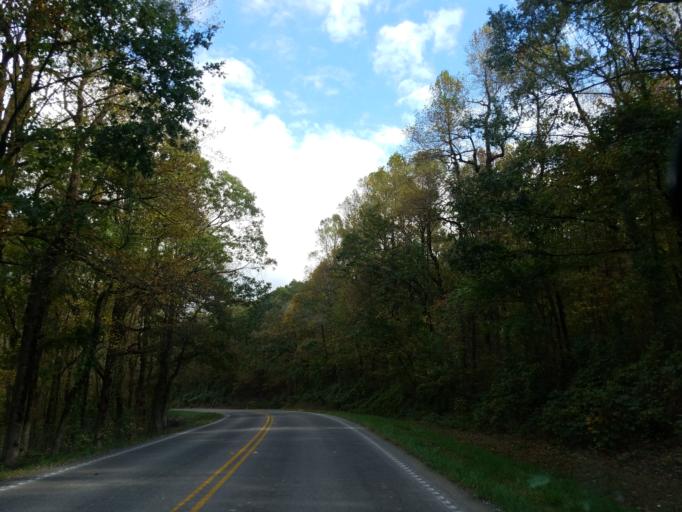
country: US
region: Georgia
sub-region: Pickens County
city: Jasper
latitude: 34.5411
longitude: -84.3504
